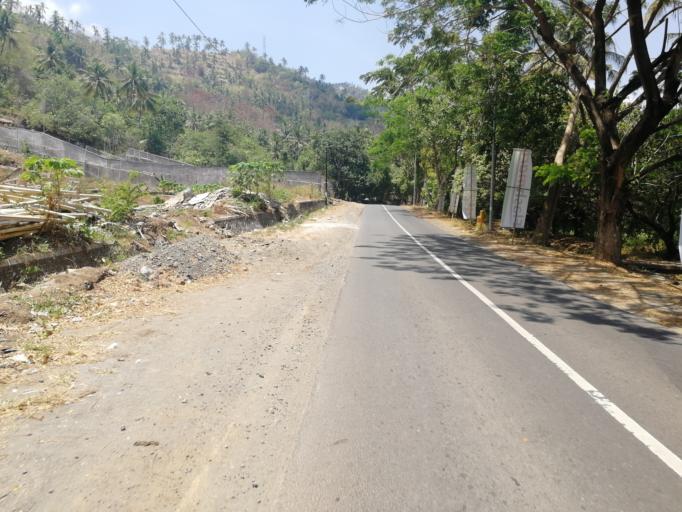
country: ID
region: West Nusa Tenggara
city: Karangsubagan
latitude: -8.4126
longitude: 116.0995
